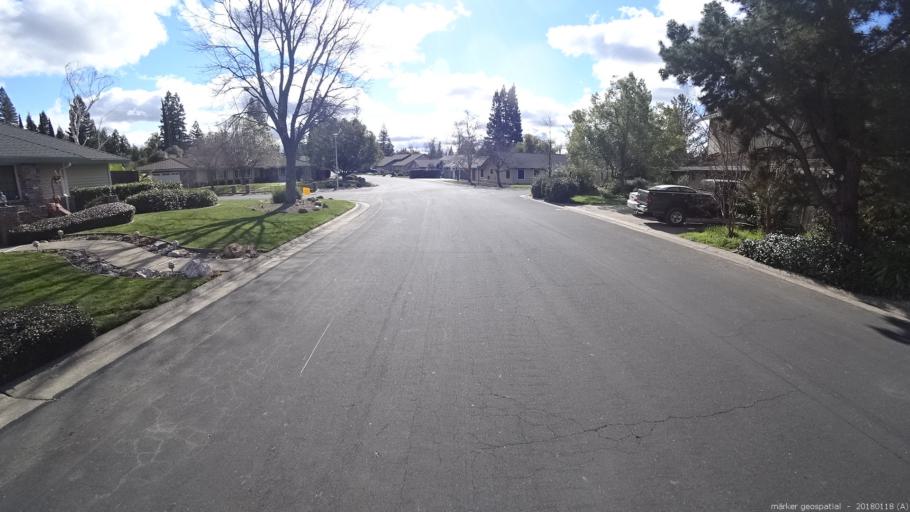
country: US
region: California
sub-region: Sacramento County
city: Folsom
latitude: 38.6883
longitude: -121.1919
